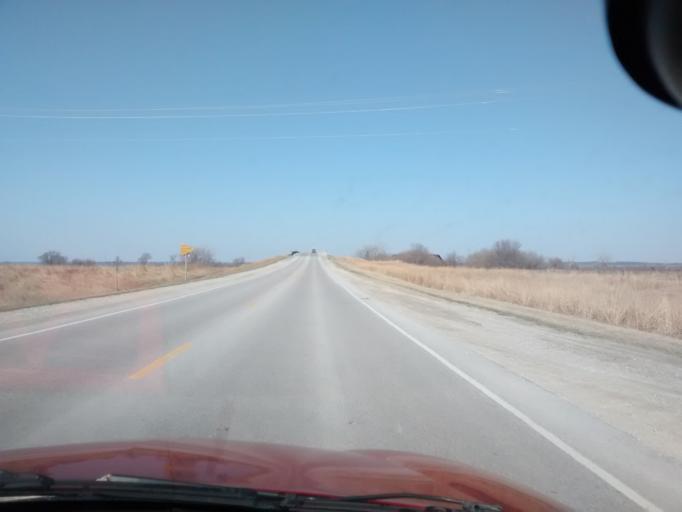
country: US
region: Iowa
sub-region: Pottawattamie County
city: Carter Lake
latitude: 41.3615
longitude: -95.8741
